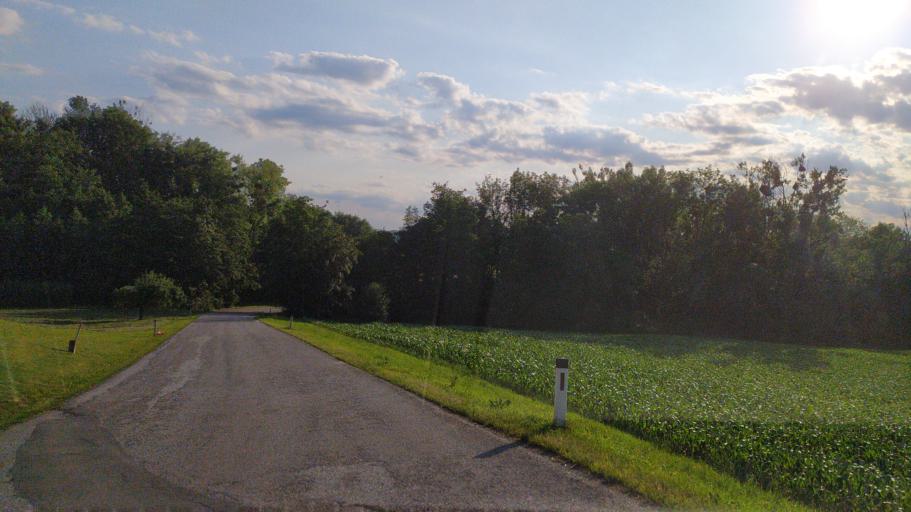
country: AT
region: Lower Austria
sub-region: Politischer Bezirk Amstetten
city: Strengberg
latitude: 48.1489
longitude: 14.6906
